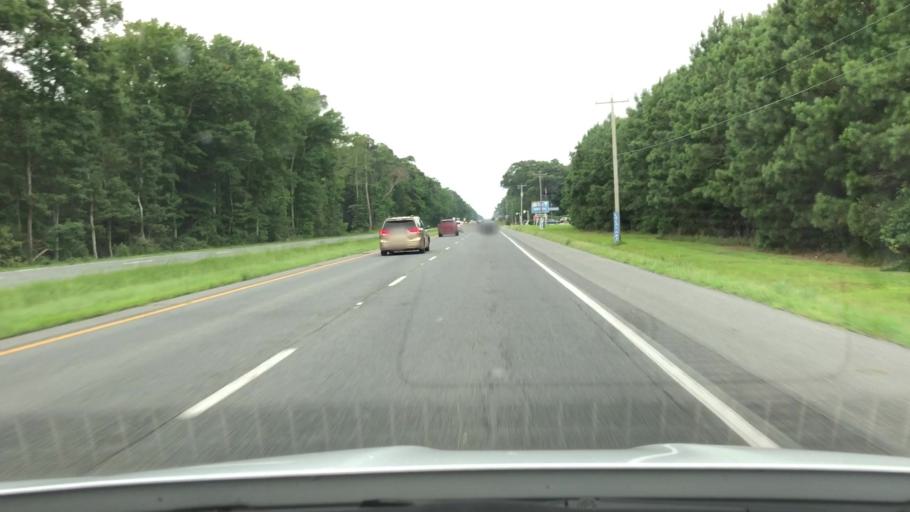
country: US
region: Virginia
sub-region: Northampton County
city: Cape Charles
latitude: 37.2050
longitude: -75.9667
